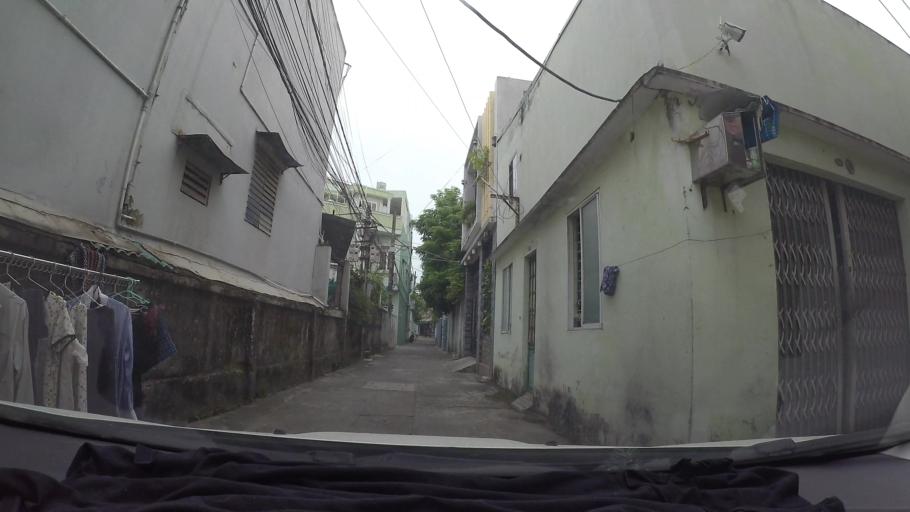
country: VN
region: Da Nang
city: Da Nang
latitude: 16.0468
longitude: 108.2088
